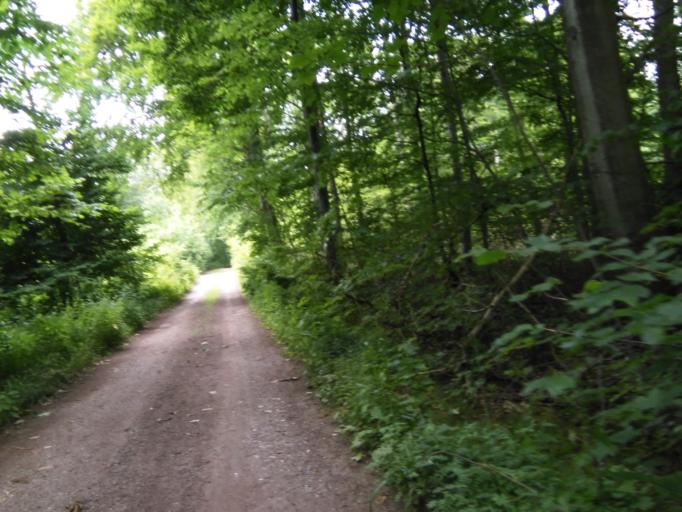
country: DK
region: Central Jutland
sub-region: Arhus Kommune
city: Solbjerg
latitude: 55.9888
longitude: 10.0822
